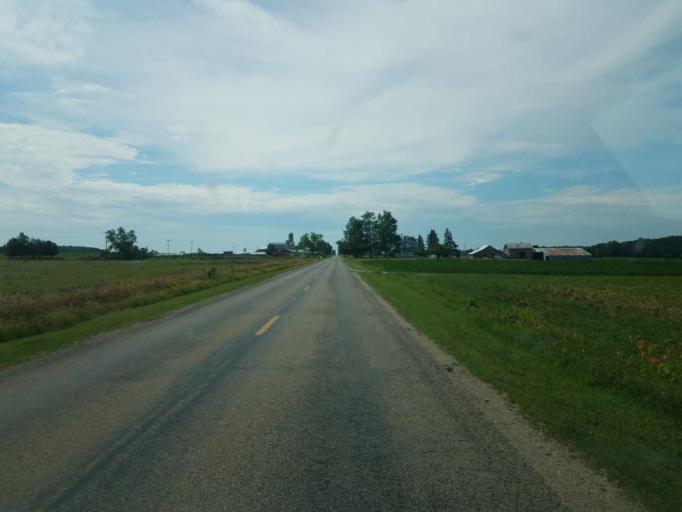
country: US
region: Michigan
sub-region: Barry County
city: Nashville
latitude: 42.6785
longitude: -84.9951
